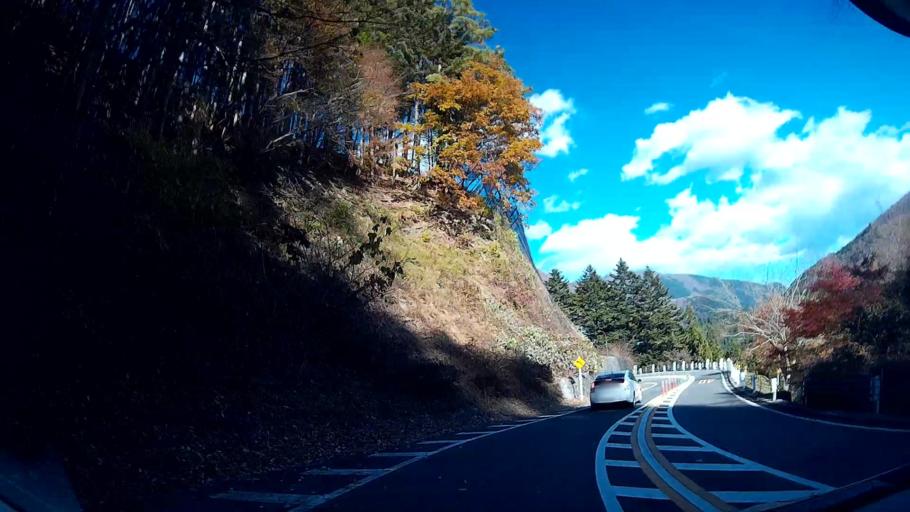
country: JP
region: Yamanashi
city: Uenohara
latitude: 35.7670
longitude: 139.0201
